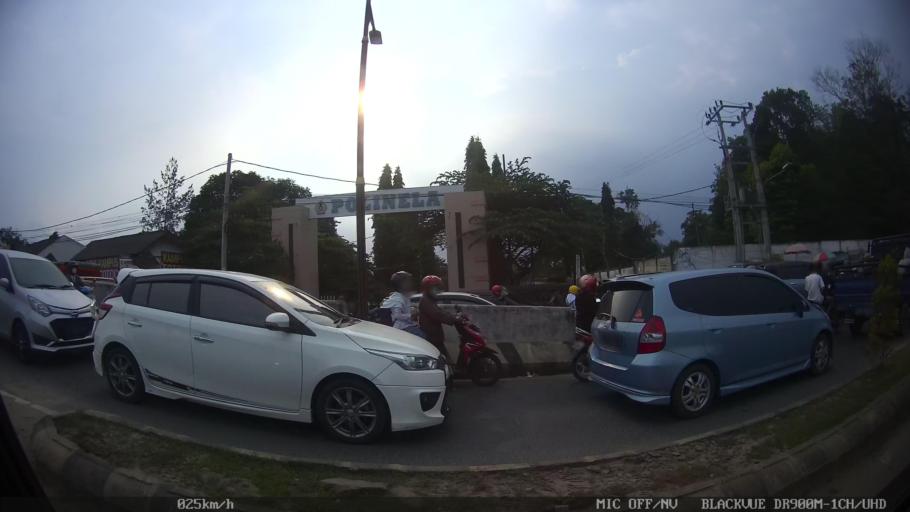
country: ID
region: Lampung
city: Kedaton
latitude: -5.3582
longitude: 105.2364
